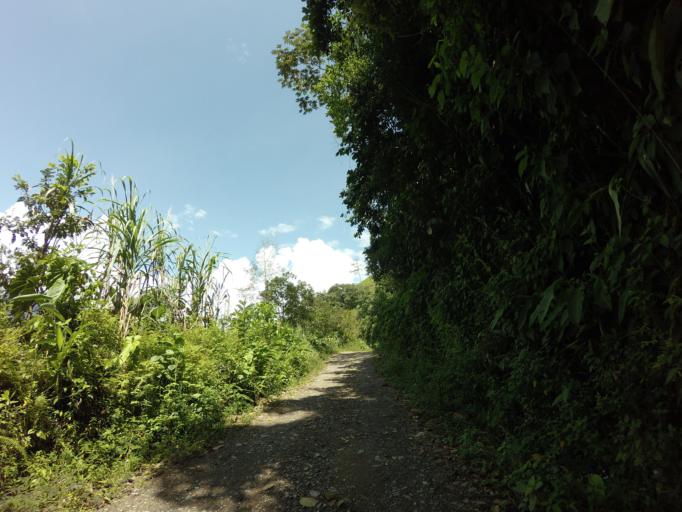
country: CO
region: Antioquia
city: Narino
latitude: 5.5130
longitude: -75.1831
